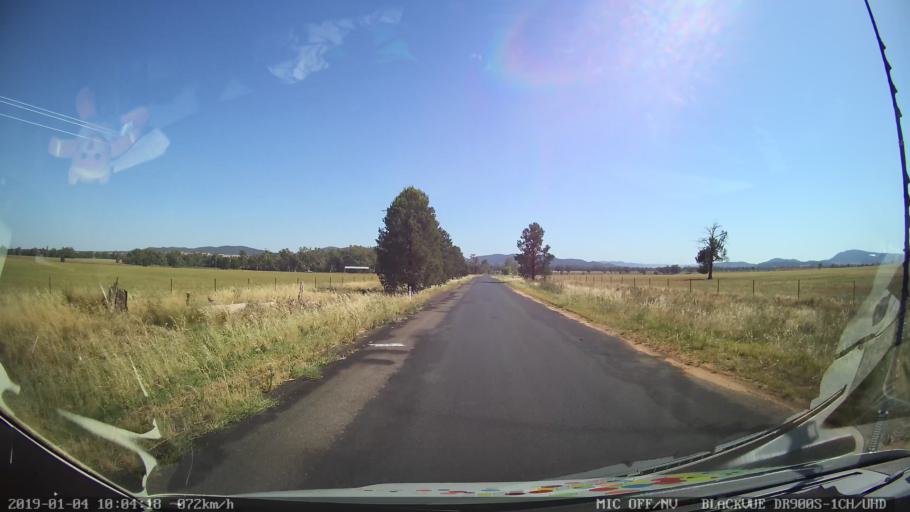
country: AU
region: New South Wales
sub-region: Cabonne
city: Canowindra
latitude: -33.4543
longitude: 148.3607
